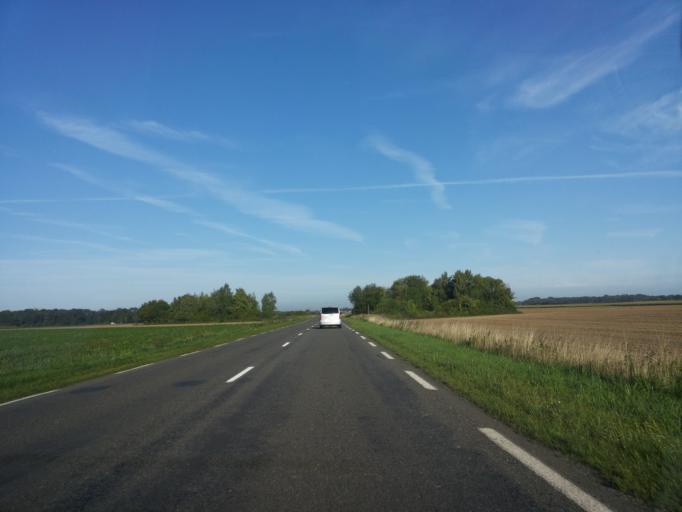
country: FR
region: Picardie
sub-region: Departement de l'Aisne
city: Athies-sous-Laon
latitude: 49.5531
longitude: 3.7141
